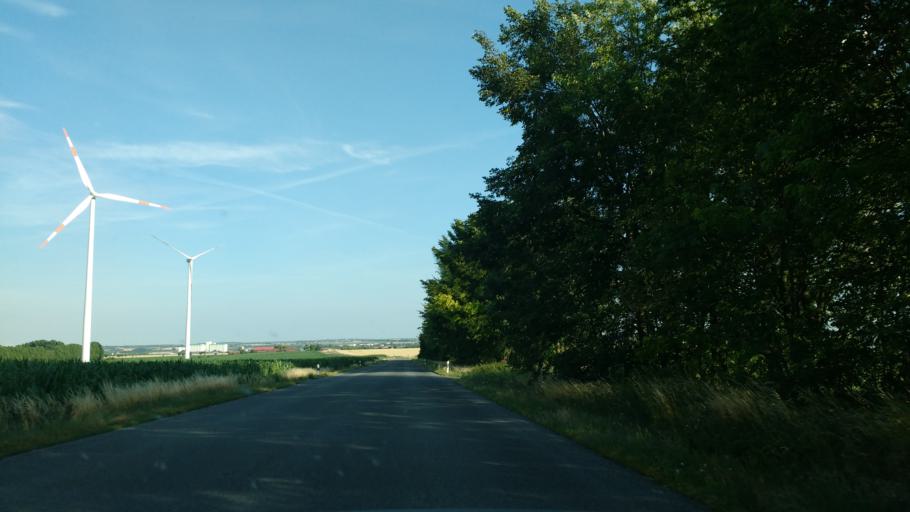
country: DE
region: Saxony-Anhalt
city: Farnstadt
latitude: 51.4135
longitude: 11.5770
